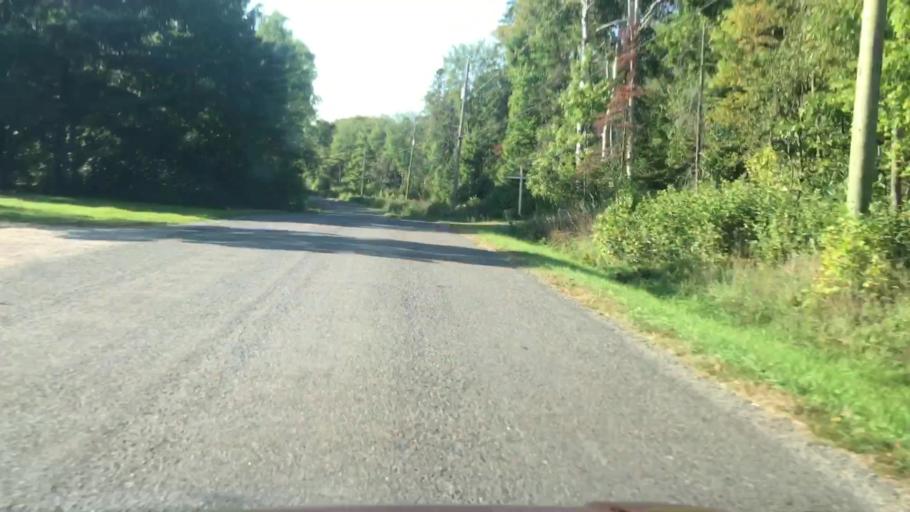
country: US
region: Michigan
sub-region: Chippewa County
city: Sault Ste. Marie
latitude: 46.2921
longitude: -84.0668
